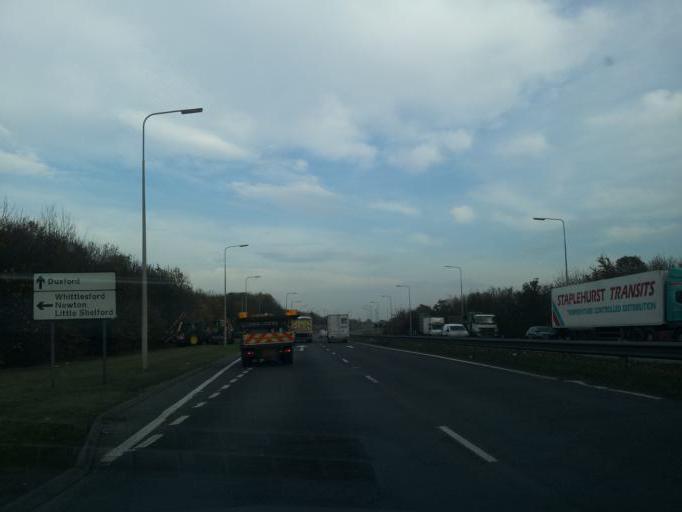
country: GB
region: England
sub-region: Cambridgeshire
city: Duxford
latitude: 52.0994
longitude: 0.1397
